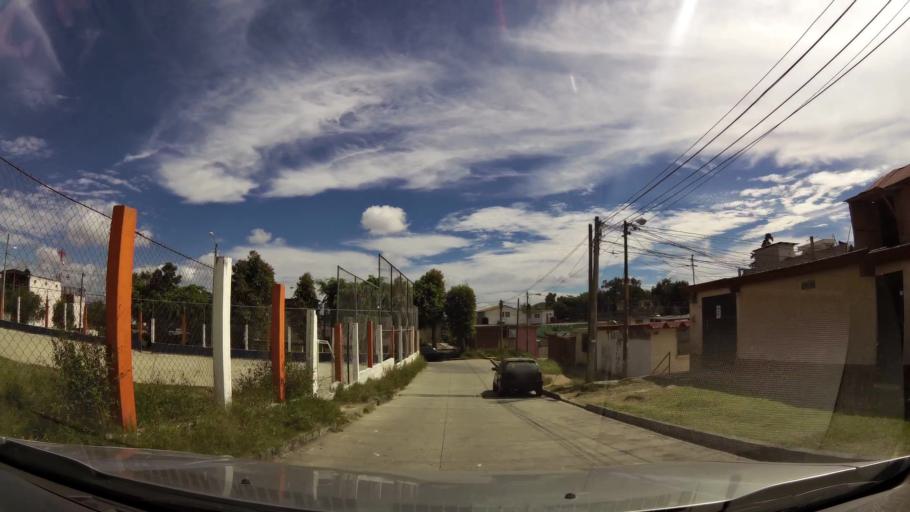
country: GT
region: Guatemala
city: Mixco
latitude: 14.6745
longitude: -90.5673
